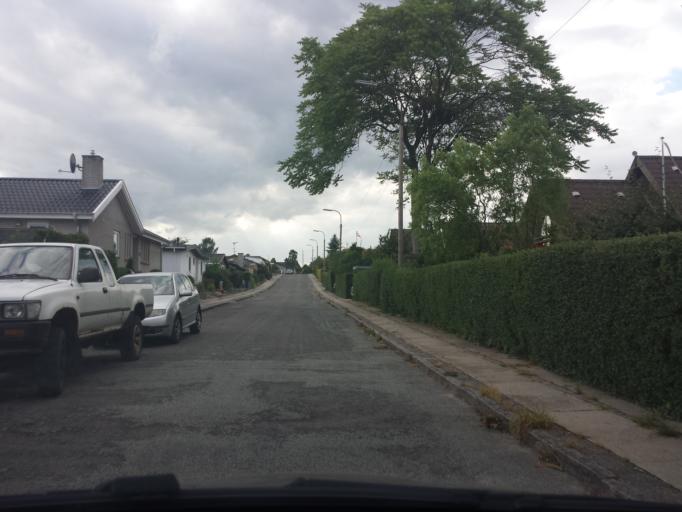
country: DK
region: Capital Region
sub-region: Herlev Kommune
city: Herlev
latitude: 55.7231
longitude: 12.4171
